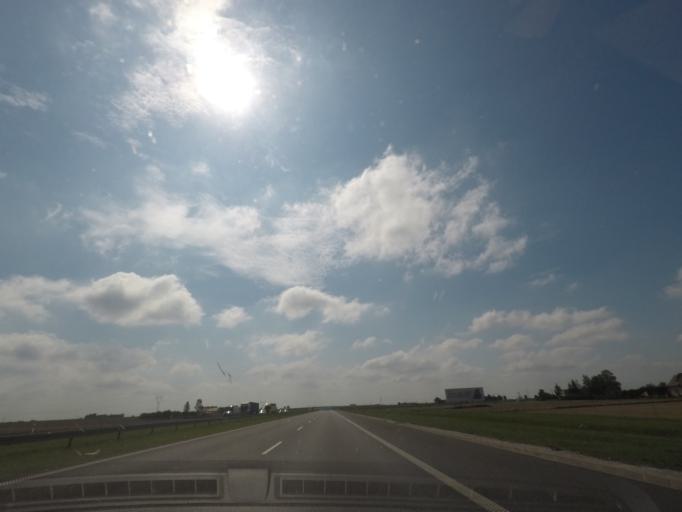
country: PL
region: Kujawsko-Pomorskie
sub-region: Powiat wloclawski
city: Lubanie
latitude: 52.7204
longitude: 18.8690
